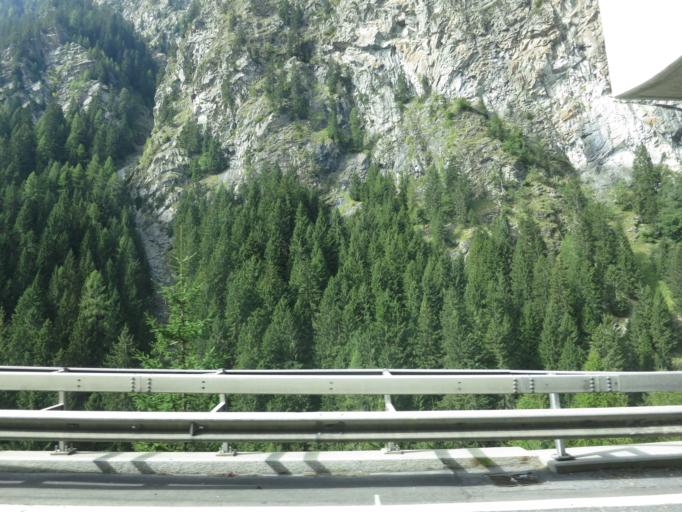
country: CH
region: Grisons
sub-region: Hinterrhein District
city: Thusis
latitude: 46.5772
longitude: 9.4177
